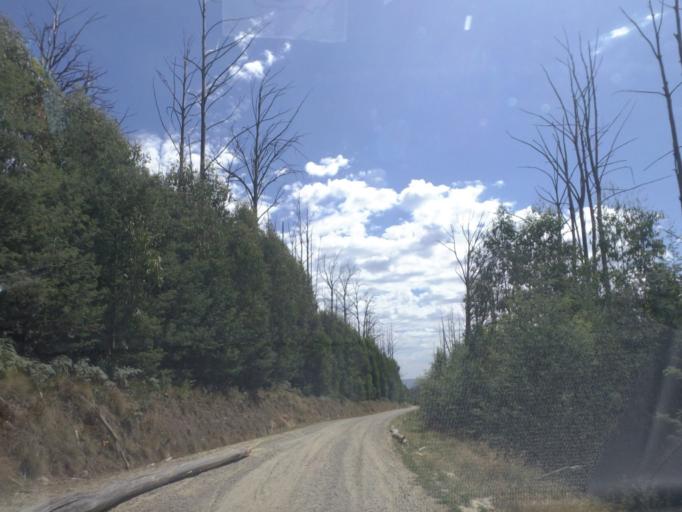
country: AU
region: Victoria
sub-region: Murrindindi
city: Alexandra
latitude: -37.4503
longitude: 145.7950
